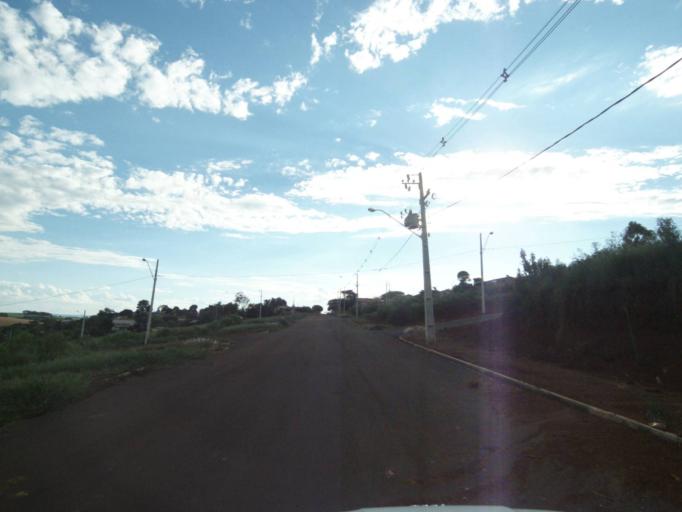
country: BR
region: Parana
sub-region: Laranjeiras Do Sul
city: Laranjeiras do Sul
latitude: -25.4901
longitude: -52.5226
